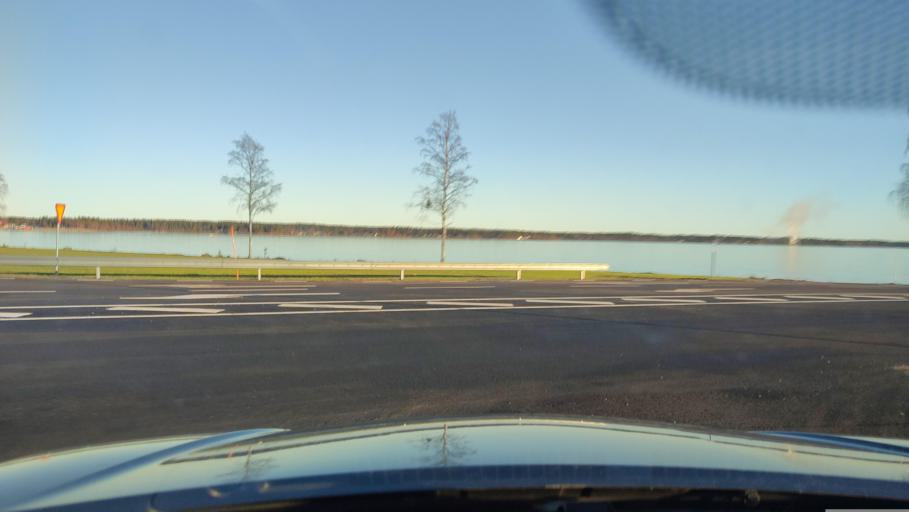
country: SE
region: Vaesterbotten
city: Obbola
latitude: 63.6866
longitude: 20.3413
